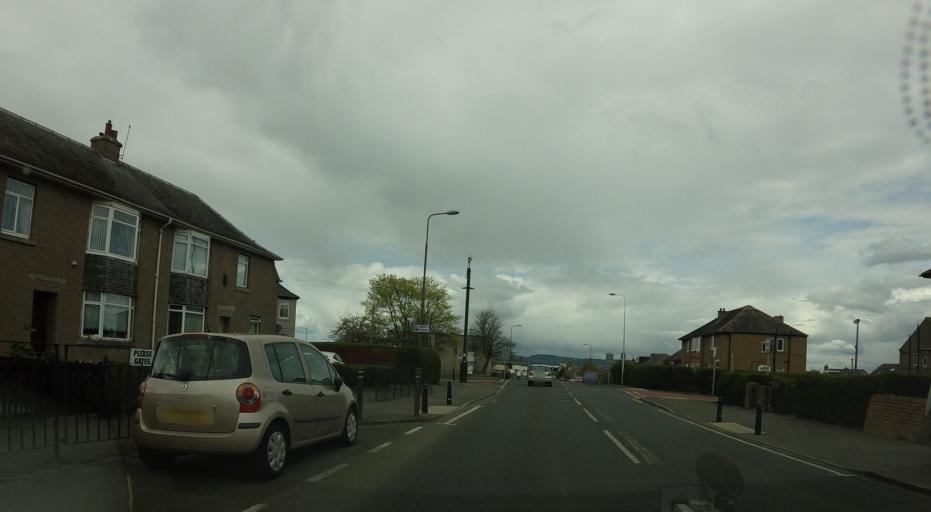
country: GB
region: Scotland
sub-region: Edinburgh
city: Edinburgh
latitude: 55.9718
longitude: -3.2379
